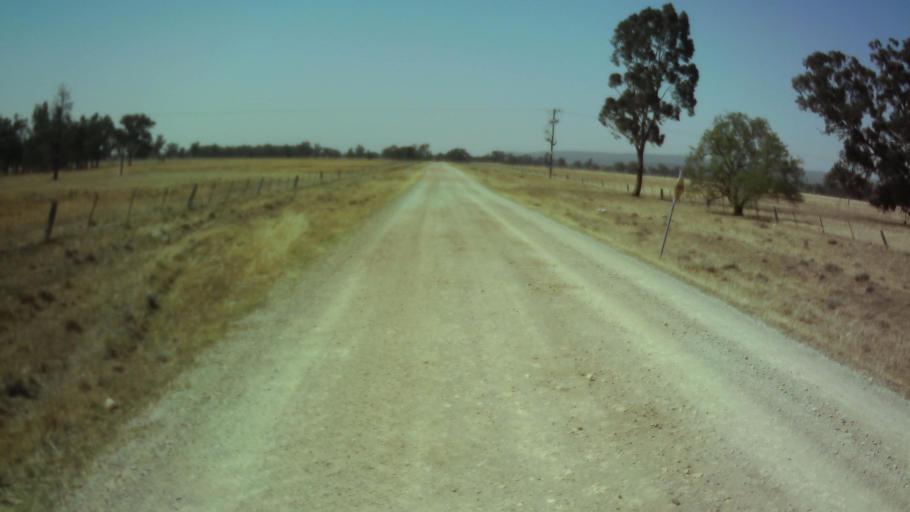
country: AU
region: New South Wales
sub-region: Weddin
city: Grenfell
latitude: -34.0329
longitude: 147.9121
